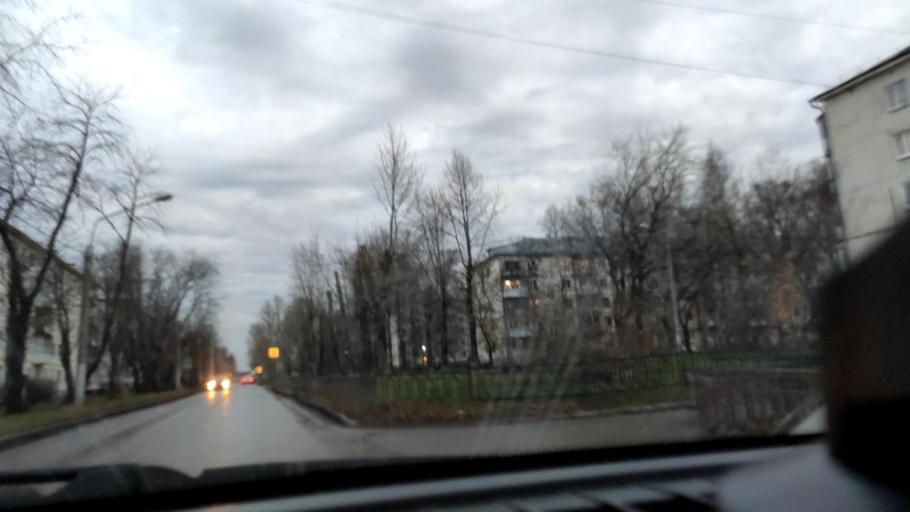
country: RU
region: Perm
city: Perm
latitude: 57.9960
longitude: 56.2967
